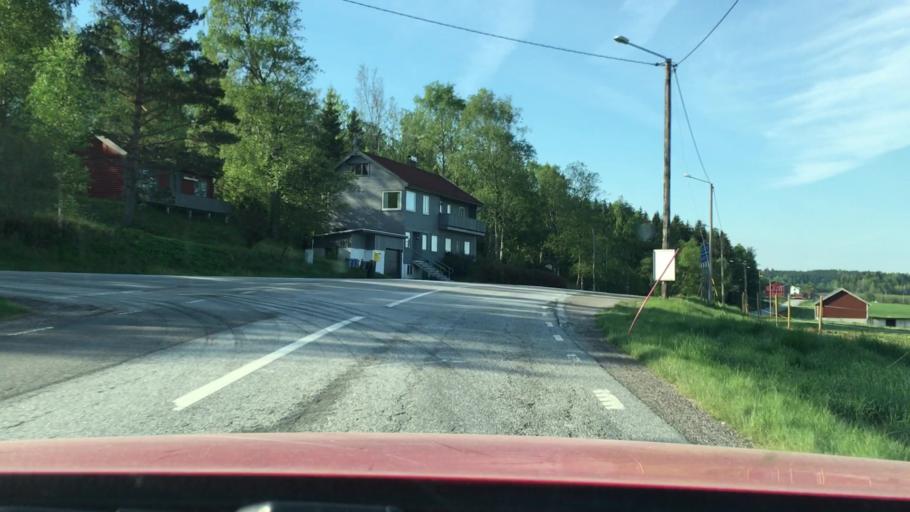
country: SE
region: Vaestra Goetaland
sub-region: Munkedals Kommun
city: Munkedal
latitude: 58.6053
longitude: 11.5591
